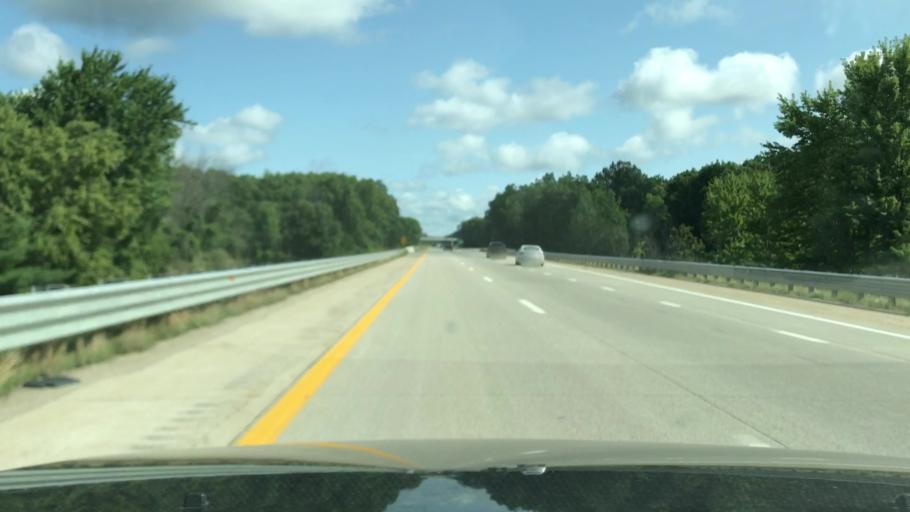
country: US
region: Michigan
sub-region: Montcalm County
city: Howard City
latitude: 43.3889
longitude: -85.5161
